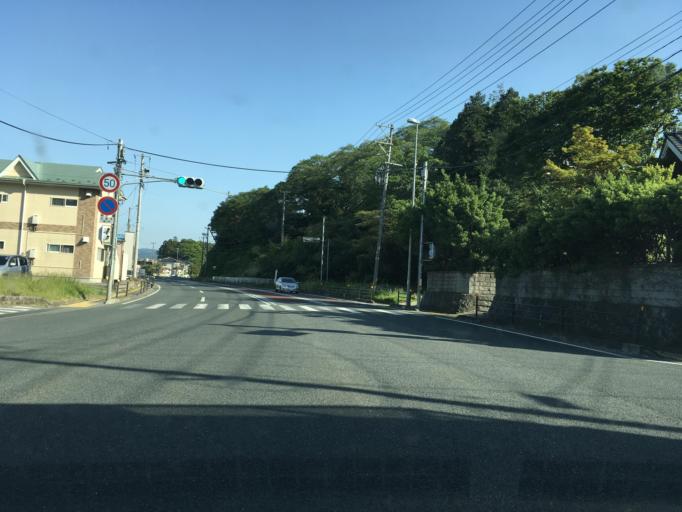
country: JP
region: Iwate
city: Ofunato
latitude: 39.0834
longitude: 141.7083
